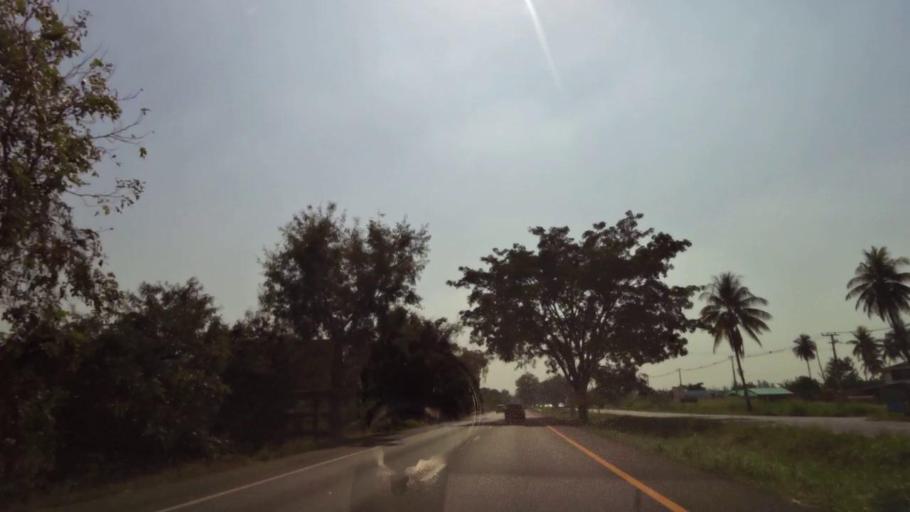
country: TH
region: Phichit
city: Bueng Na Rang
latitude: 16.0391
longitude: 100.1175
